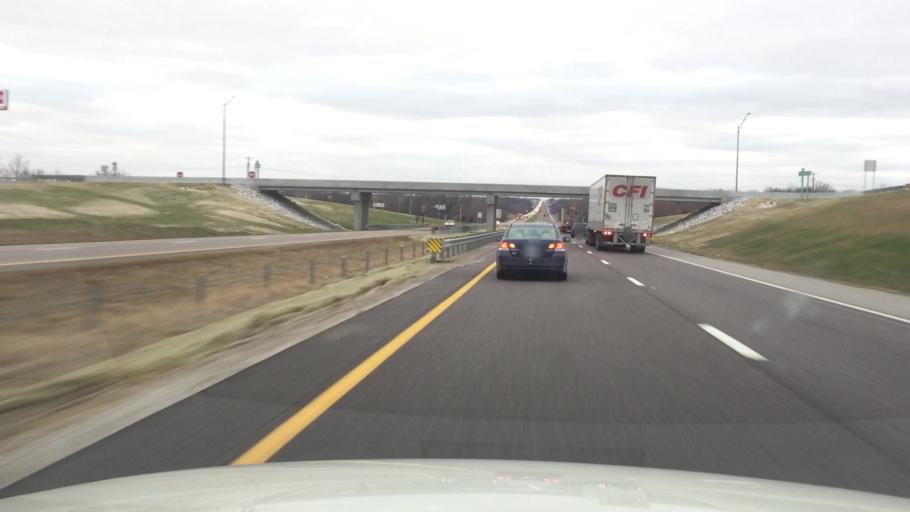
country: US
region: Missouri
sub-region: Cooper County
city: Boonville
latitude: 38.9377
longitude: -92.6898
